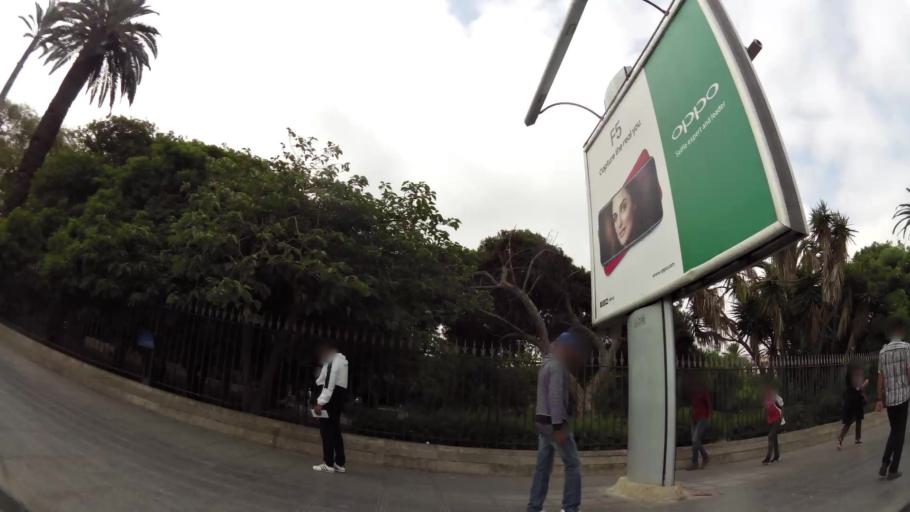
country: MA
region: Rabat-Sale-Zemmour-Zaer
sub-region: Rabat
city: Rabat
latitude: 34.0233
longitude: -6.8346
